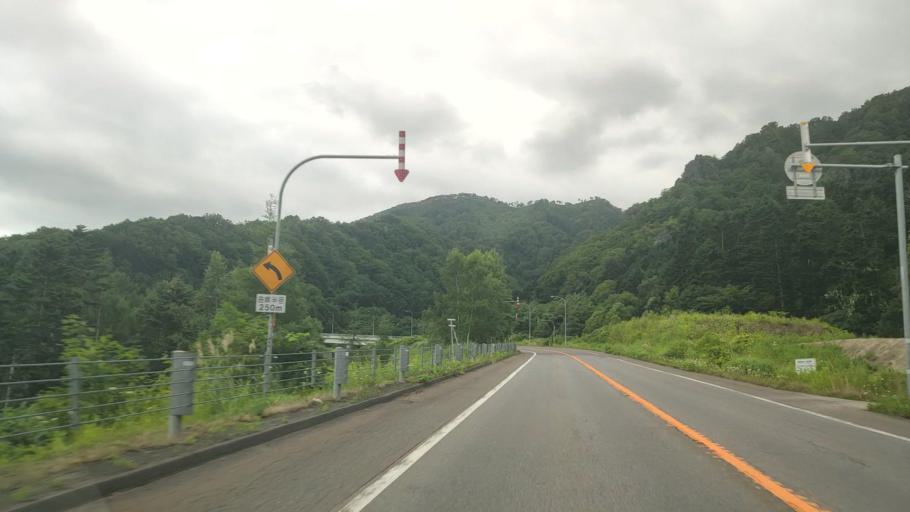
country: JP
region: Hokkaido
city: Niseko Town
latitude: 42.6045
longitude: 140.5639
